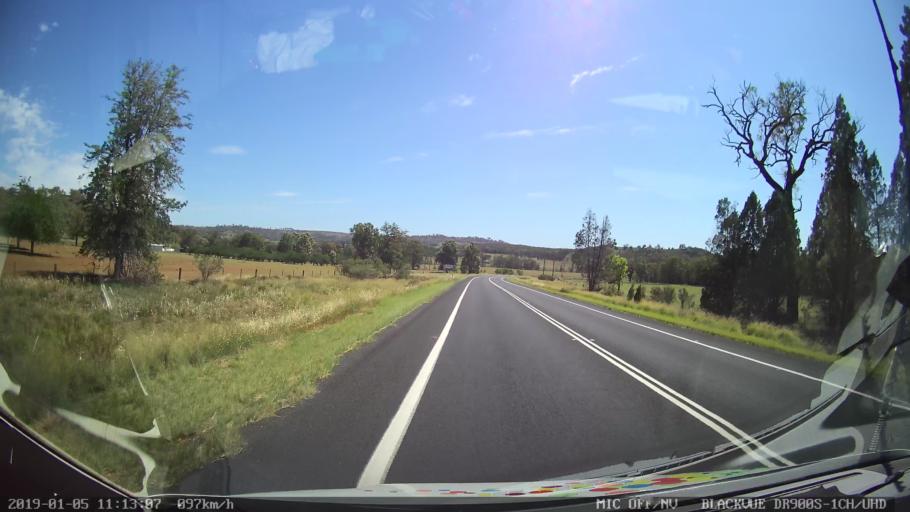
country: AU
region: New South Wales
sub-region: Warrumbungle Shire
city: Coonabarabran
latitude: -31.3742
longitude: 149.2672
